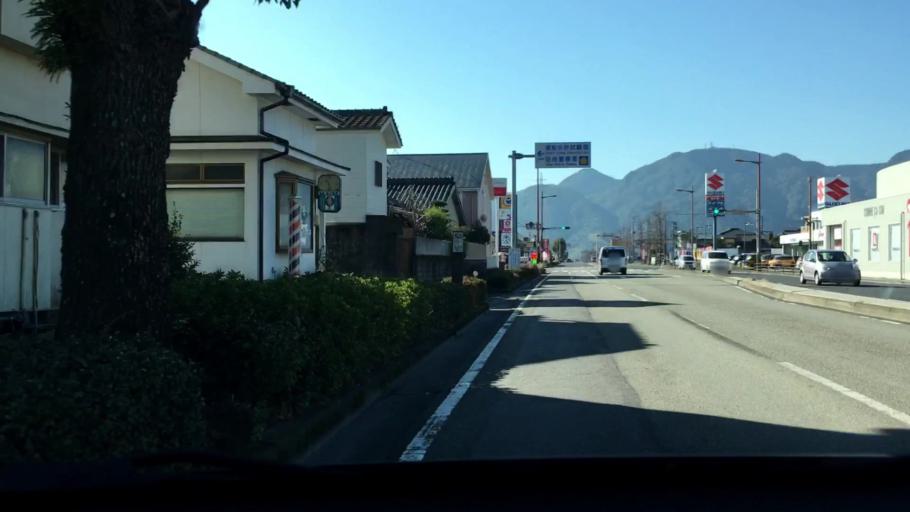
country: JP
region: Kagoshima
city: Kajiki
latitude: 31.7268
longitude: 130.6245
